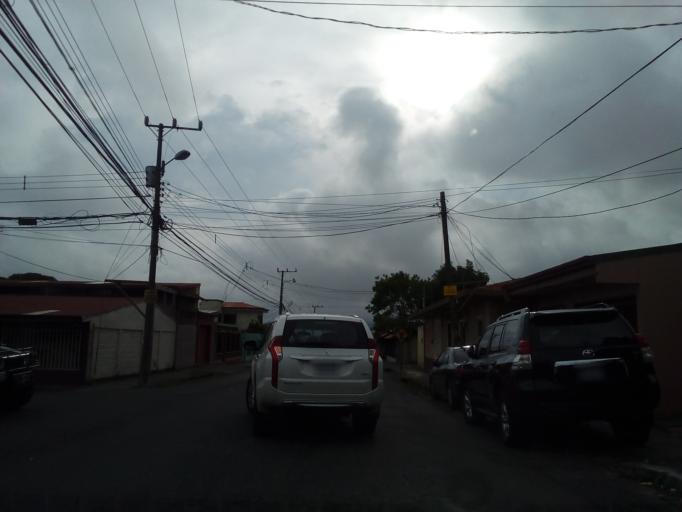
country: CR
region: Heredia
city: San Pablo
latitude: 9.9835
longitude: -84.0865
